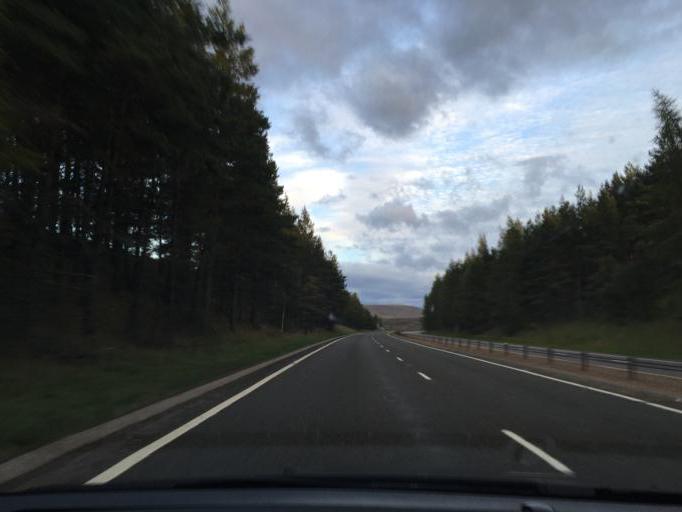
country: GB
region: Scotland
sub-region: Highland
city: Aviemore
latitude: 57.3394
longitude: -3.9874
